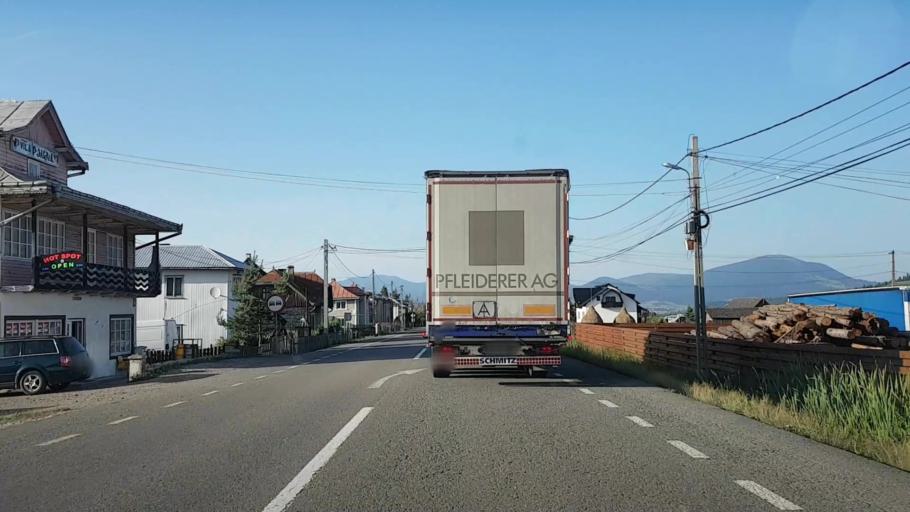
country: RO
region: Suceava
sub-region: Comuna Poiana Stampei
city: Poiana Stampei
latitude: 47.3125
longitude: 25.1298
